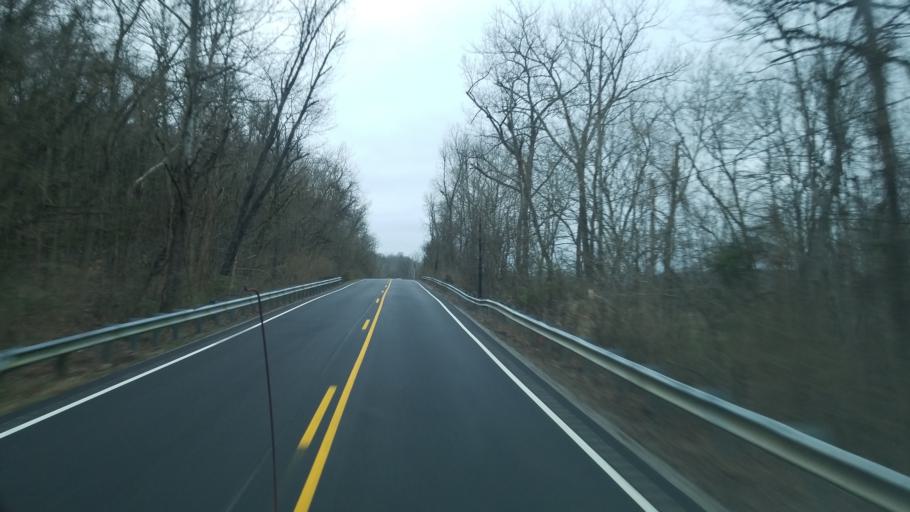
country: US
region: Kentucky
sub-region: Bracken County
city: Augusta
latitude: 38.7772
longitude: -83.9611
